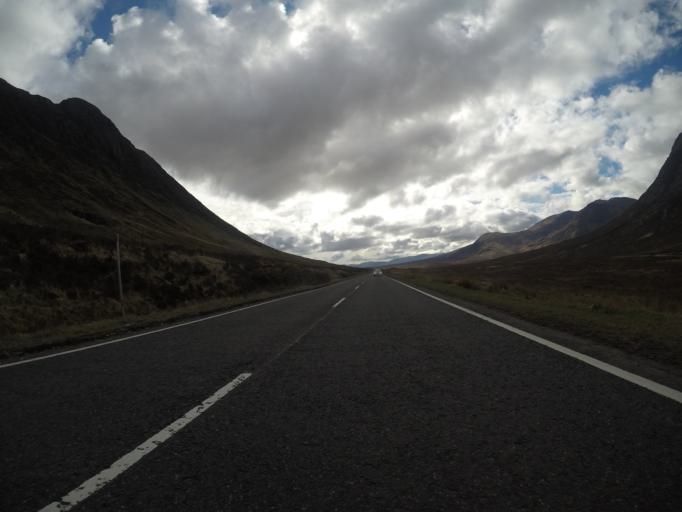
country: GB
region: Scotland
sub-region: Highland
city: Spean Bridge
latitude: 56.6631
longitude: -4.8975
